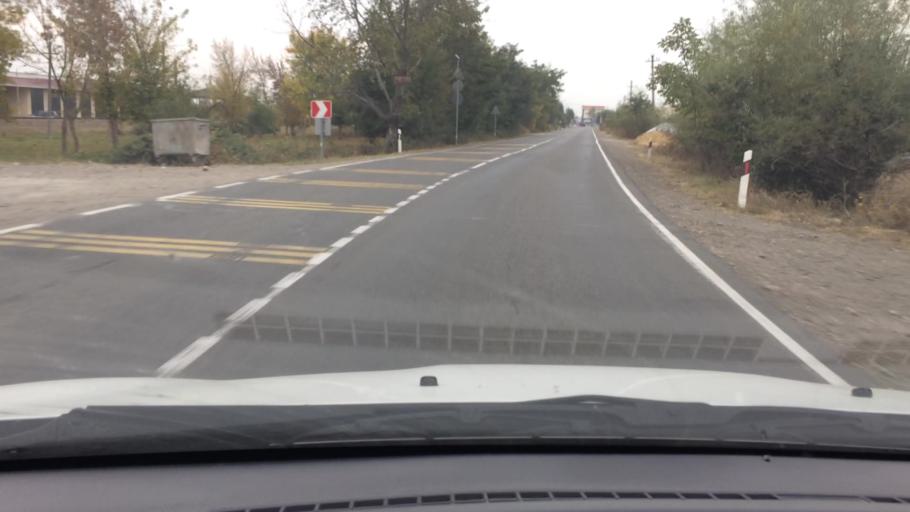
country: GE
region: Kvemo Kartli
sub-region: Marneuli
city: Marneuli
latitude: 41.4640
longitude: 44.8086
